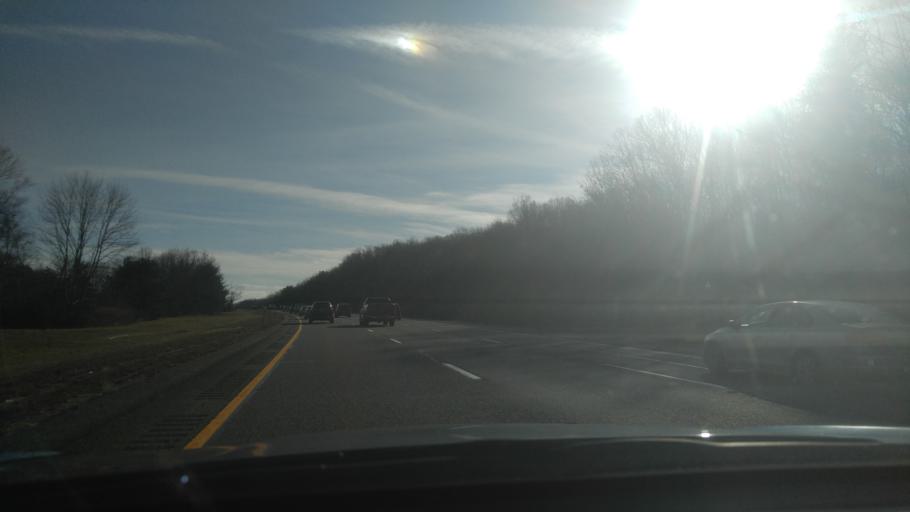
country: US
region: Rhode Island
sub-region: Providence County
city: Greenville
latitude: 41.8932
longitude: -71.5233
